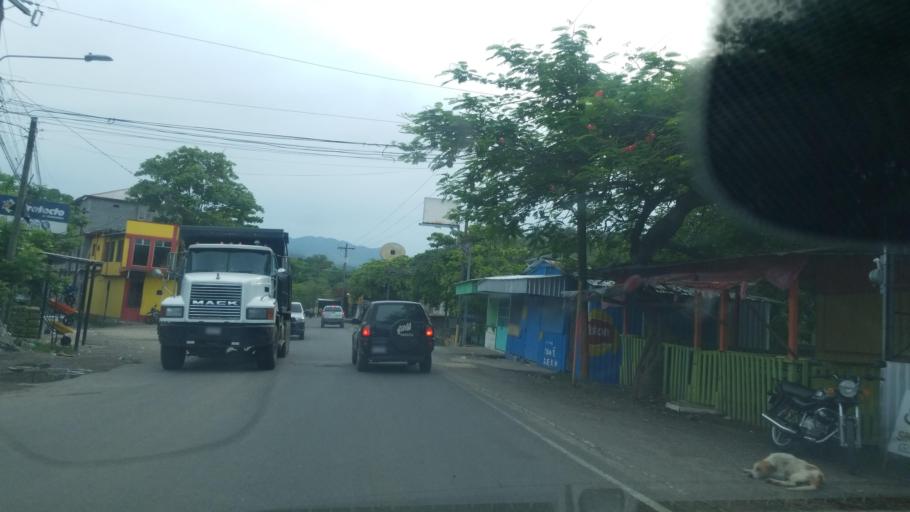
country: HN
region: Santa Barbara
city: Santa Barbara
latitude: 14.9203
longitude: -88.2446
